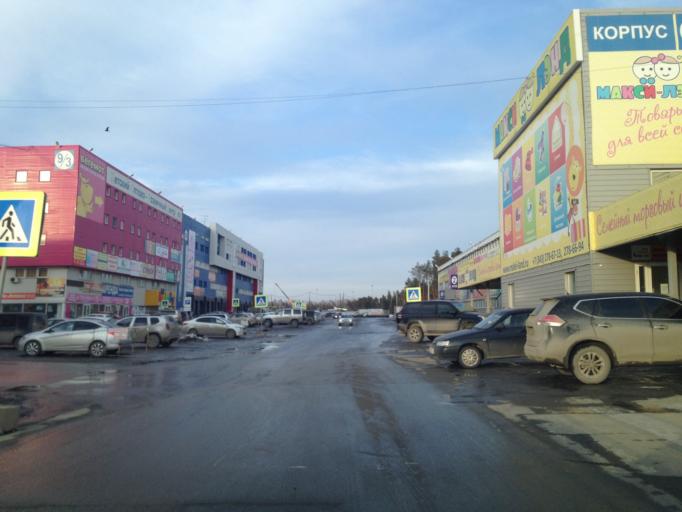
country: RU
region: Sverdlovsk
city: Istok
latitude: 56.7565
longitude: 60.7560
